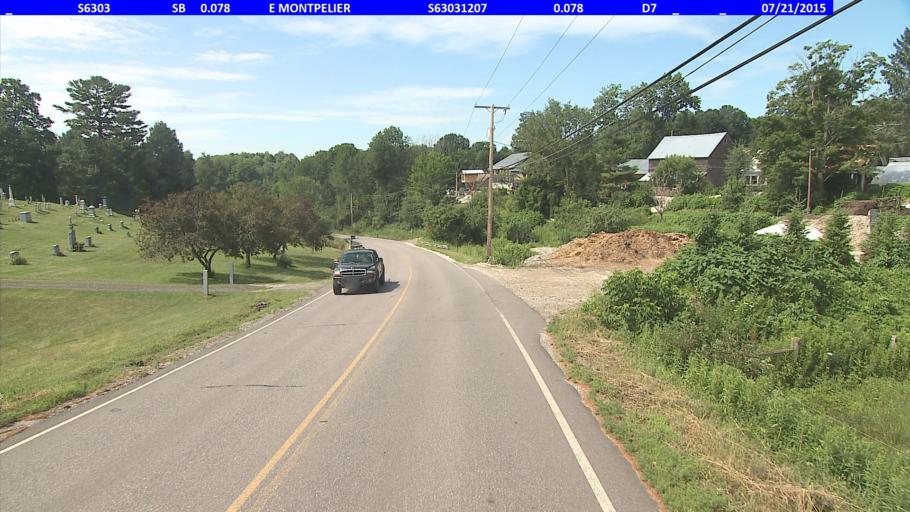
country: US
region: Vermont
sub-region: Washington County
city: Montpelier
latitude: 44.2734
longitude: -72.5558
